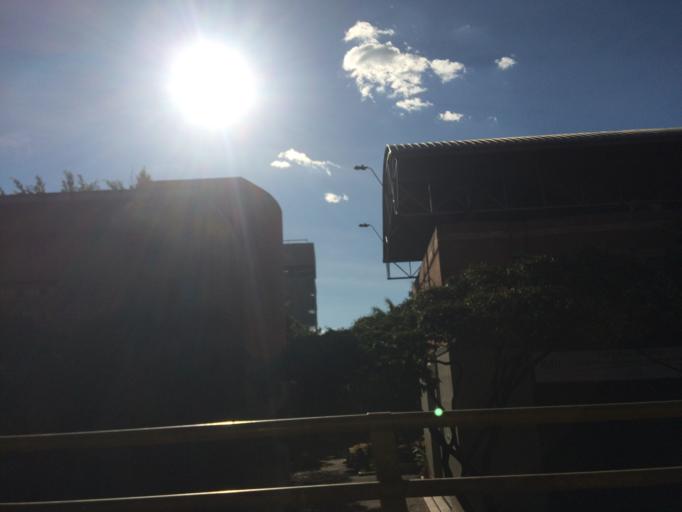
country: CO
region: Antioquia
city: Medellin
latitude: 6.2448
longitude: -75.5680
